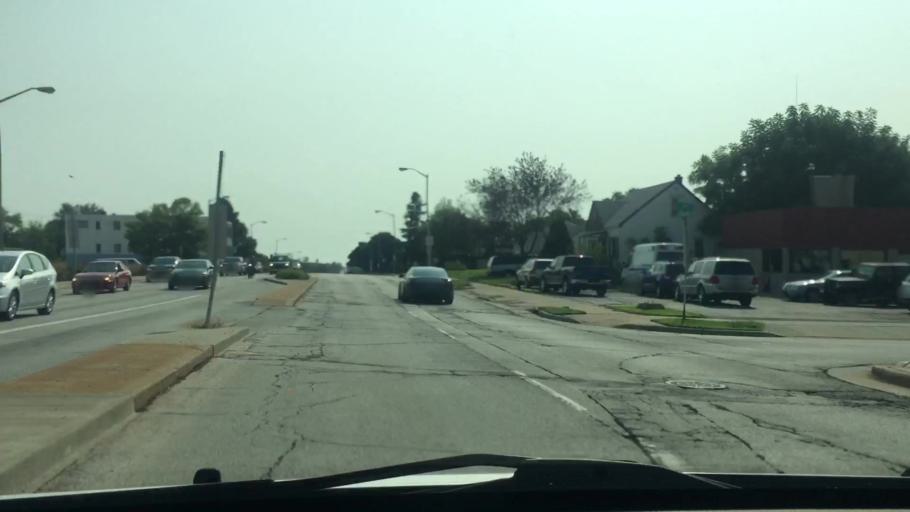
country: US
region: Wisconsin
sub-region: Milwaukee County
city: West Allis
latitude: 43.0026
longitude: -88.0311
